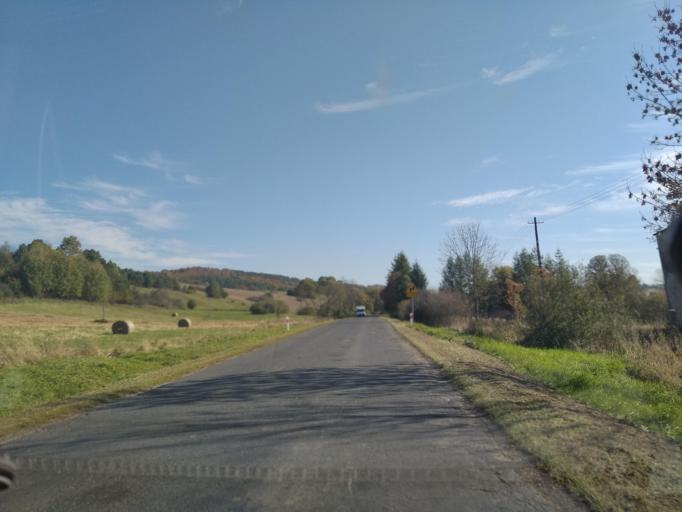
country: PL
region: Subcarpathian Voivodeship
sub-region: Powiat sanocki
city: Bukowsko
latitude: 49.4144
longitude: 21.9717
